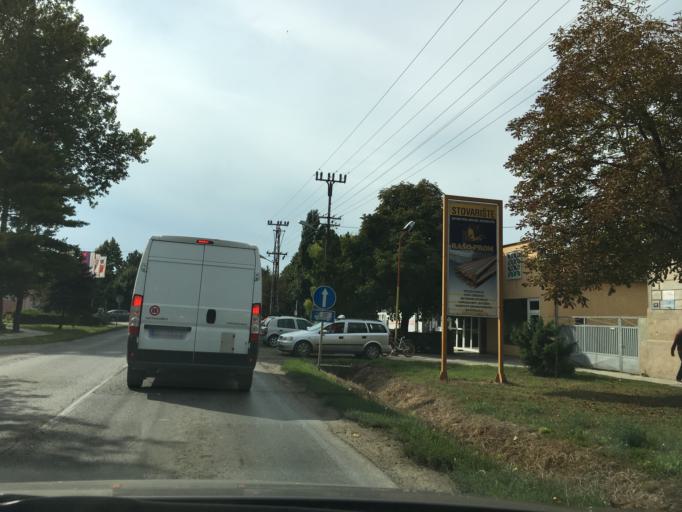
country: RS
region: Autonomna Pokrajina Vojvodina
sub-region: Juznobacki Okrug
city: Temerin
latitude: 45.3726
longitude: 19.8734
